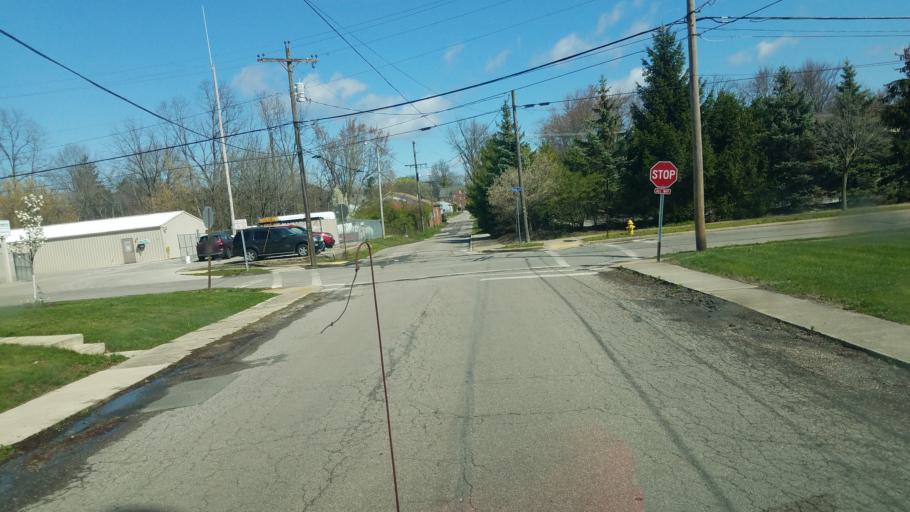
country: US
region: Ohio
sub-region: Delaware County
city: Delaware
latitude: 40.2931
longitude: -83.0766
